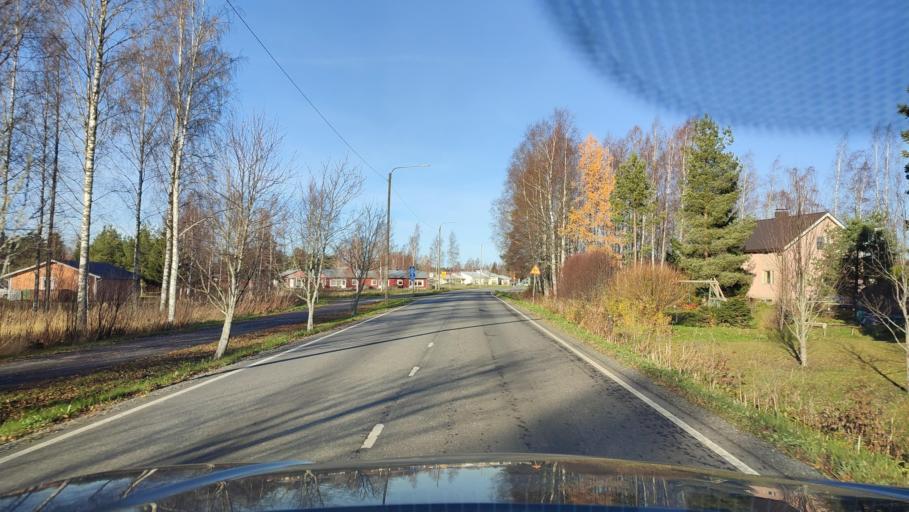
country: FI
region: Southern Ostrobothnia
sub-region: Suupohja
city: Karijoki
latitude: 62.3036
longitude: 21.7111
